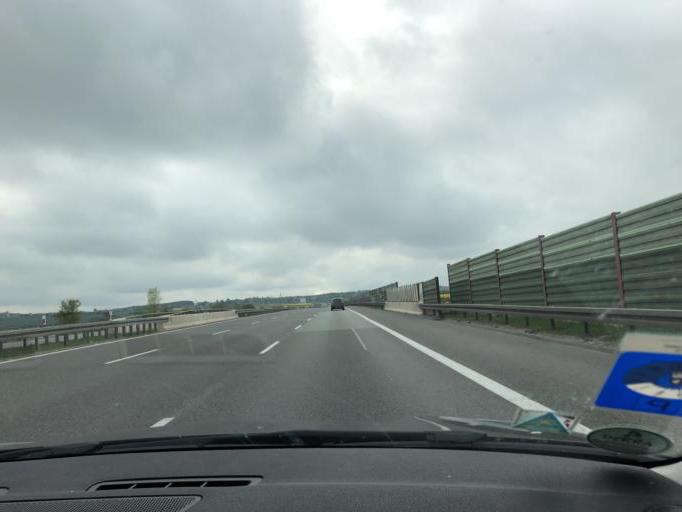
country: PL
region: Opole Voivodeship
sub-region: Powiat strzelecki
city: Lesnica
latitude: 50.4666
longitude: 18.1969
